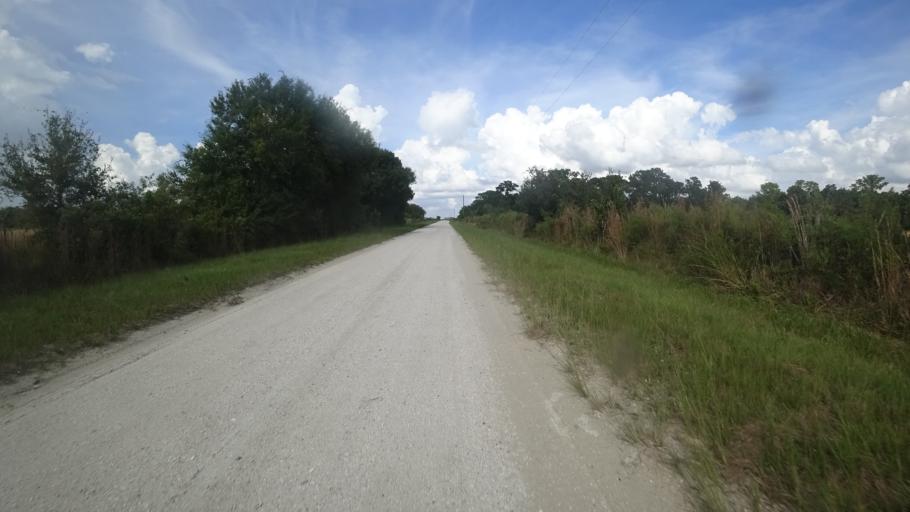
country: US
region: Florida
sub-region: Hillsborough County
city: Wimauma
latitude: 27.5707
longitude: -82.1741
